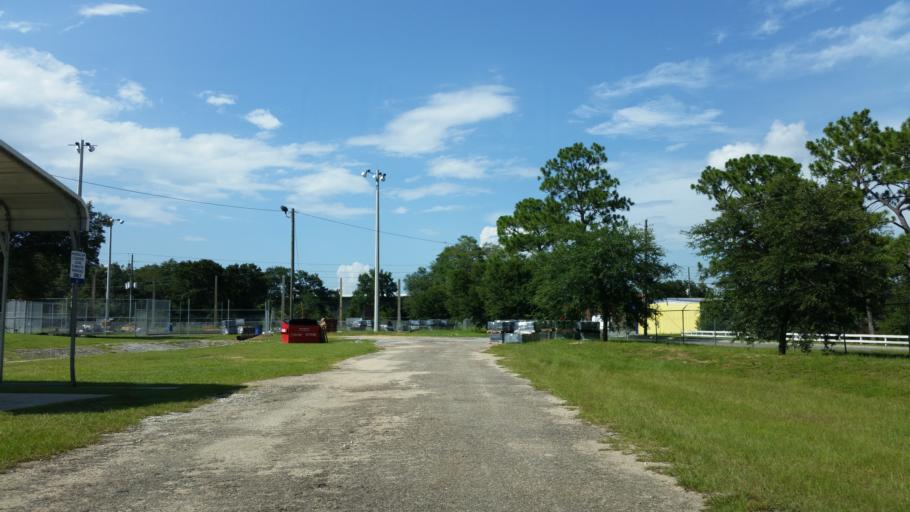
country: US
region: Florida
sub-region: Escambia County
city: Ensley
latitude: 30.5313
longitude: -87.2501
